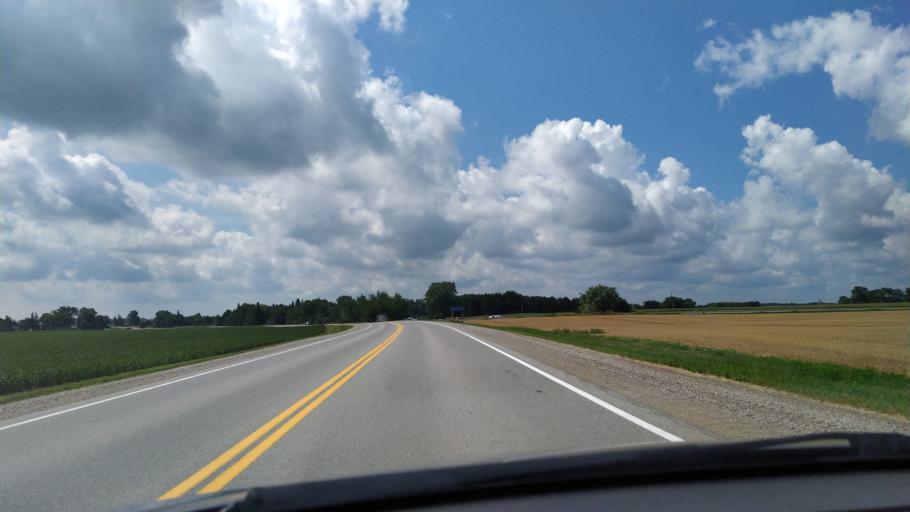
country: CA
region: Ontario
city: South Huron
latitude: 43.2685
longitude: -81.3598
